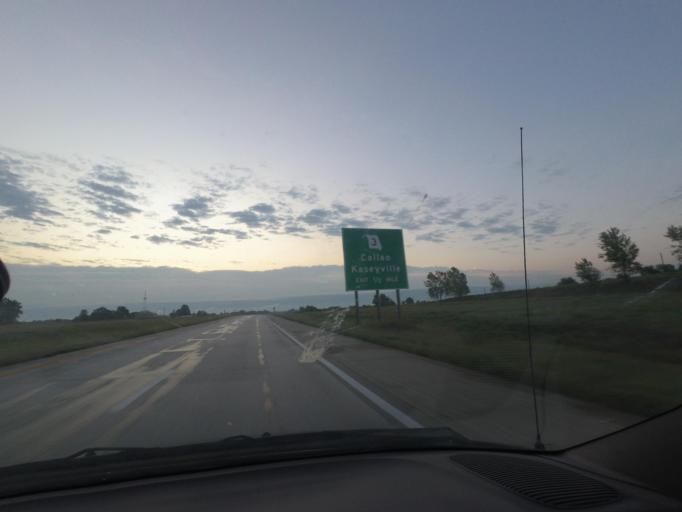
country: US
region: Missouri
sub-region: Macon County
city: Macon
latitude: 39.7583
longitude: -92.6432
